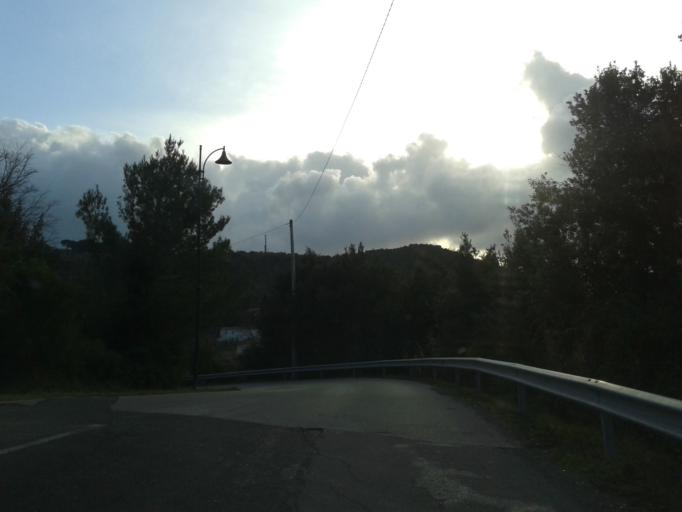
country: IT
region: Tuscany
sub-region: Provincia di Livorno
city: Quercianella
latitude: 43.4977
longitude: 10.3552
